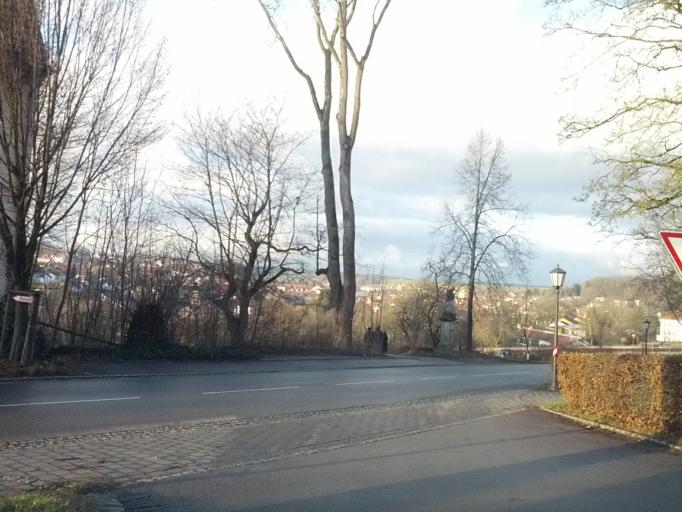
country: DE
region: Baden-Wuerttemberg
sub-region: Tuebingen Region
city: Ochsenhausen
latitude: 48.0646
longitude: 9.9490
